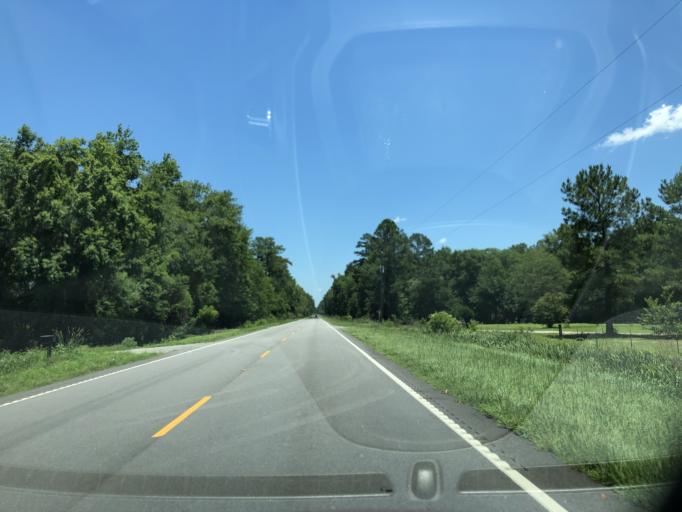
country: US
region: South Carolina
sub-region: Orangeburg County
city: Branchville
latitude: 33.2453
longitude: -80.8442
